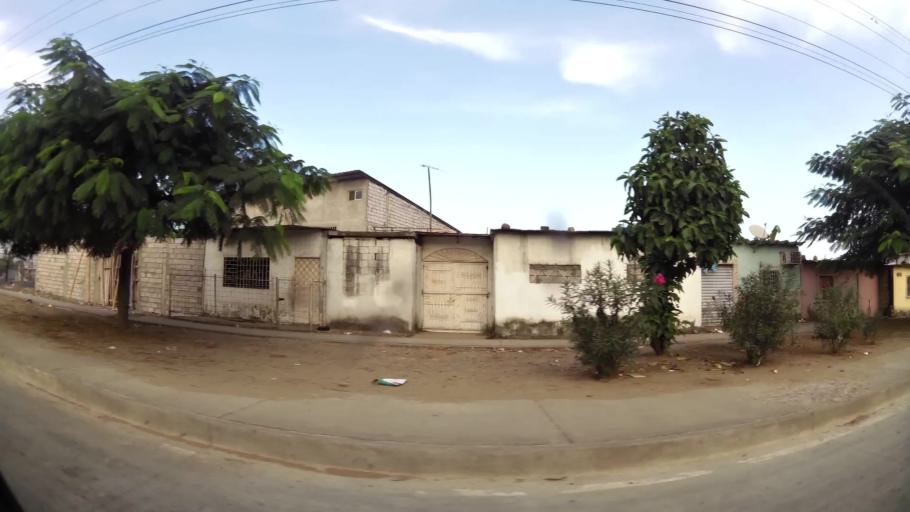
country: EC
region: Guayas
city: Eloy Alfaro
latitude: -2.0859
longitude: -79.8971
